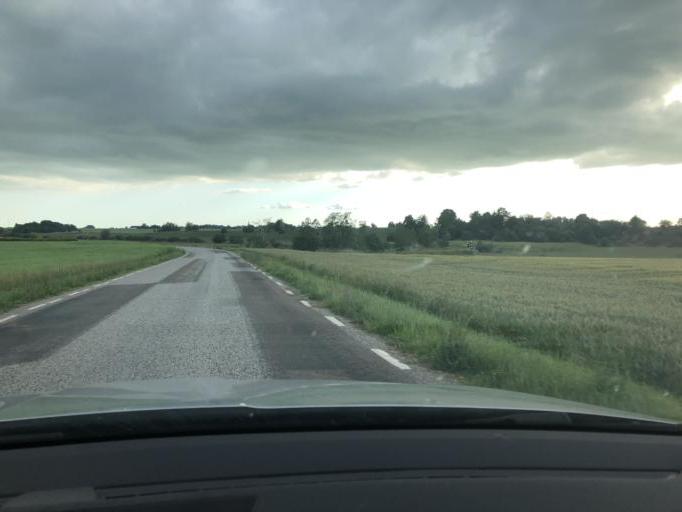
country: SE
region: Skane
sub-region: Simrishamns Kommun
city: Simrishamn
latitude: 55.5080
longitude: 14.2278
